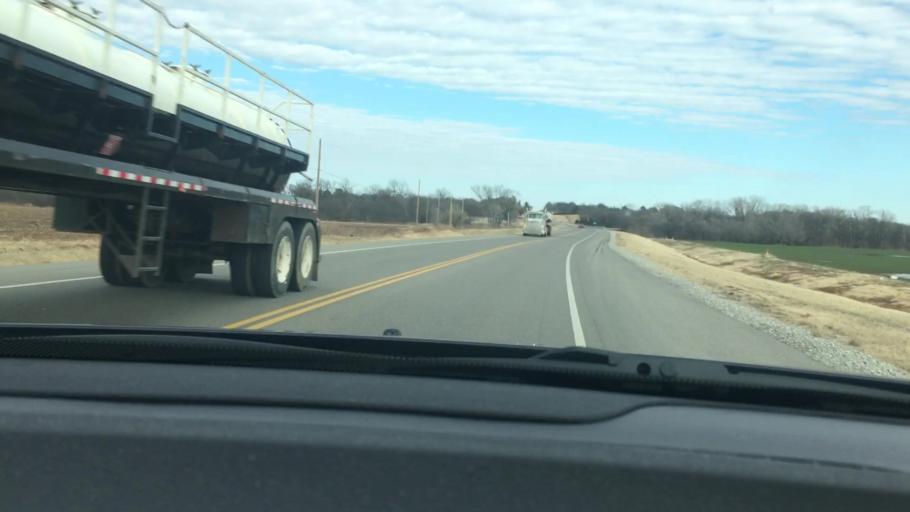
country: US
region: Oklahoma
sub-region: Garvin County
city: Pauls Valley
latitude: 34.7574
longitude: -97.2015
